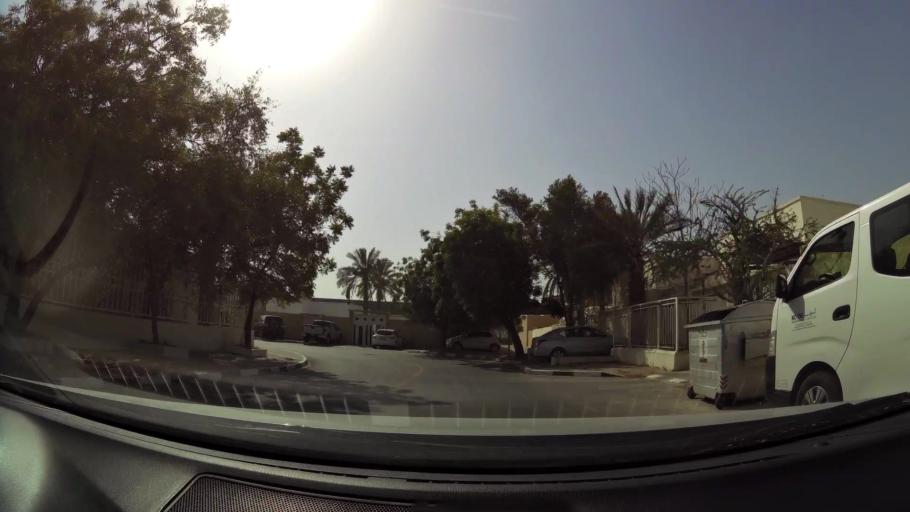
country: AE
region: Dubai
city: Dubai
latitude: 25.1706
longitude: 55.2448
